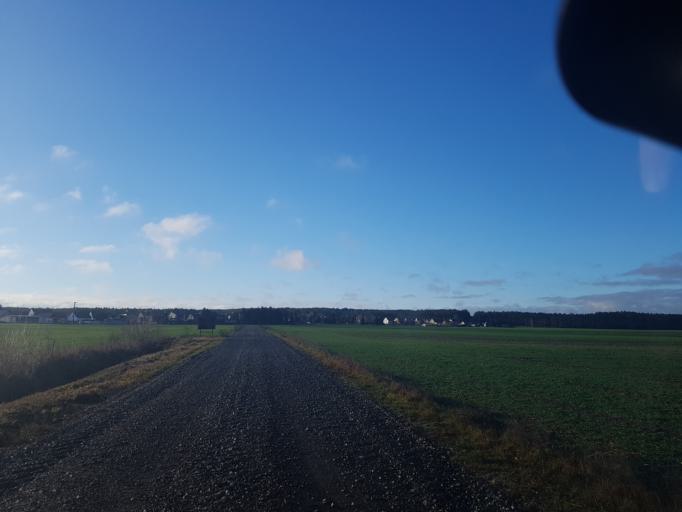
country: DE
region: Brandenburg
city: Schonborn
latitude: 51.5459
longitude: 13.4701
